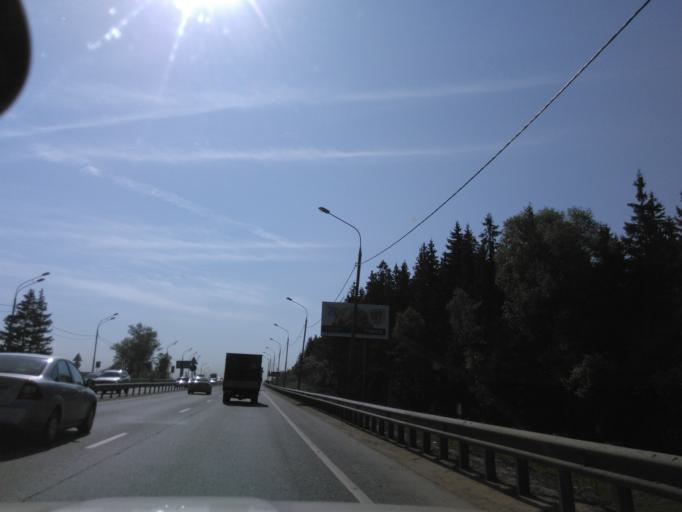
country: RU
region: Moskovskaya
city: Rzhavki
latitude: 55.9931
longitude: 37.2616
